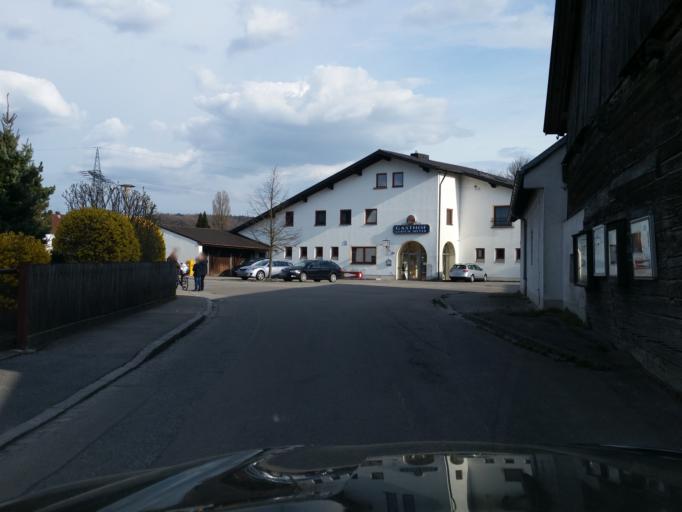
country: DE
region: Bavaria
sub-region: Lower Bavaria
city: Landshut
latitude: 48.5511
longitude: 12.1664
